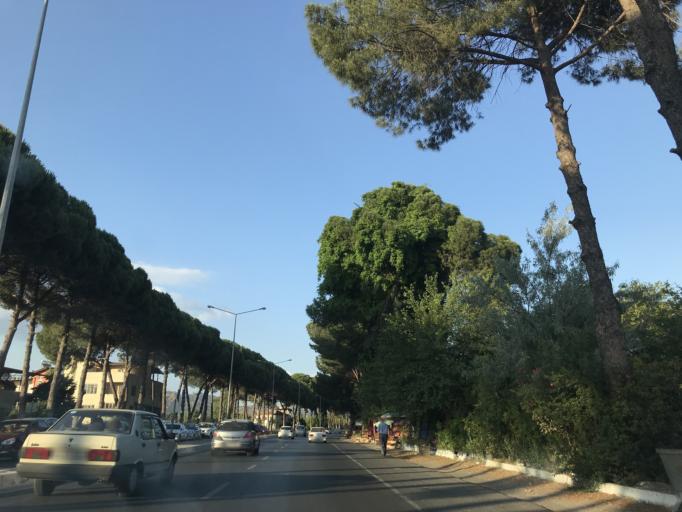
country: TR
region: Aydin
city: Sultanhisar
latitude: 37.8878
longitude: 28.1606
